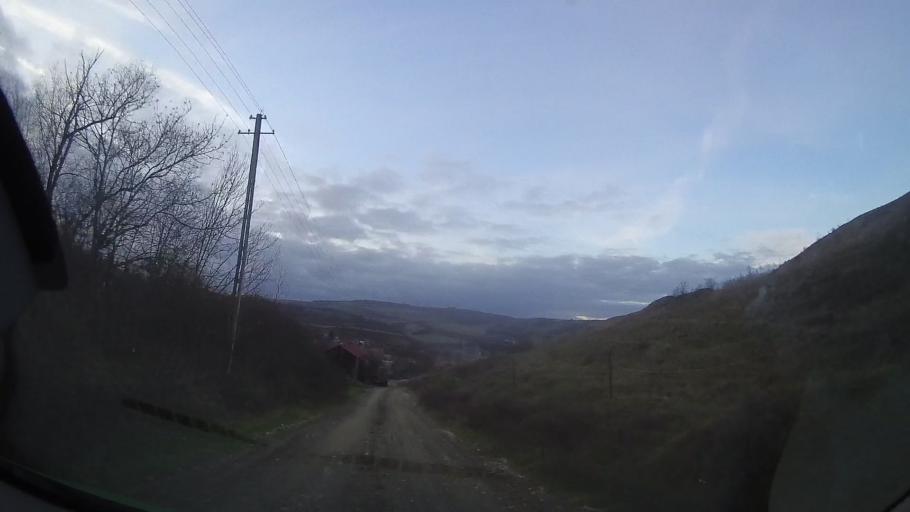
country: RO
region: Cluj
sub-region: Comuna Palatca
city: Palatca
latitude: 46.8637
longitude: 24.0206
